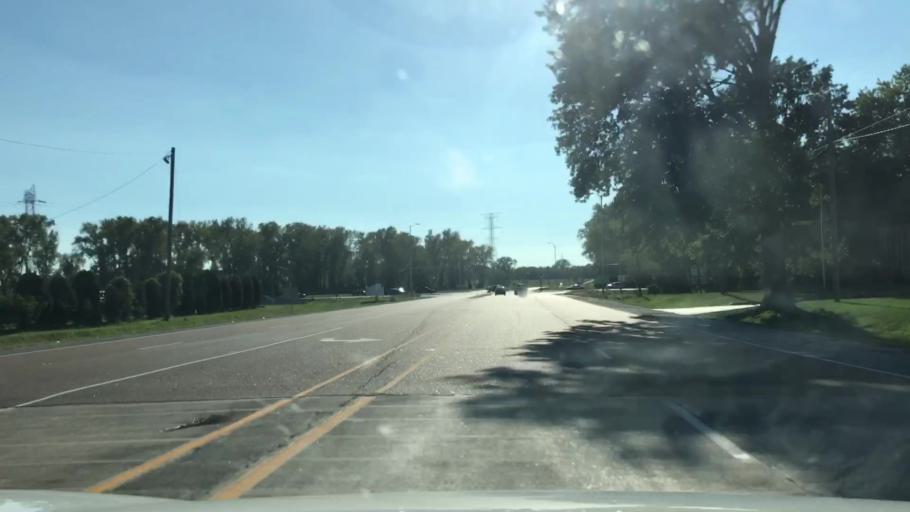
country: US
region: Illinois
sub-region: Madison County
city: Wood River
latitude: 38.8590
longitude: -90.1064
